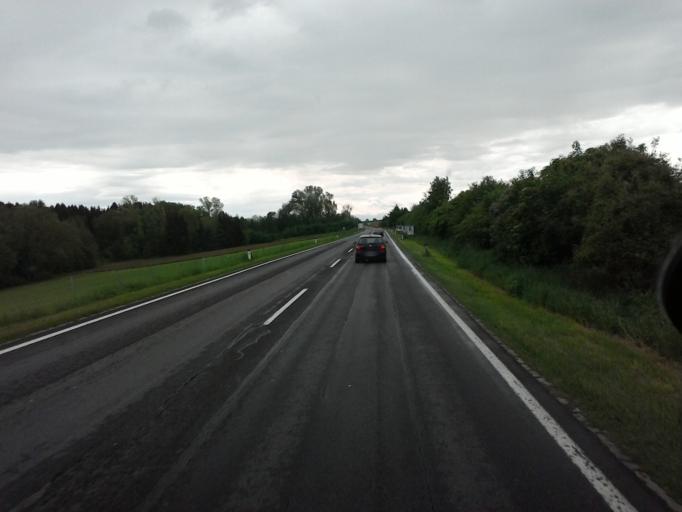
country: AT
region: Upper Austria
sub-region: Wels-Land
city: Steinhaus
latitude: 48.1230
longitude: 14.0490
